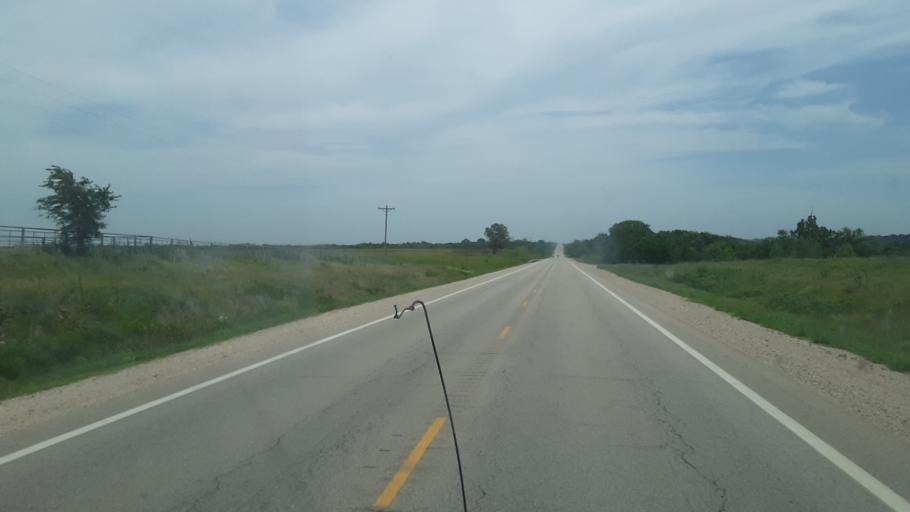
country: US
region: Kansas
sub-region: Woodson County
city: Yates Center
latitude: 37.8363
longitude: -95.9420
